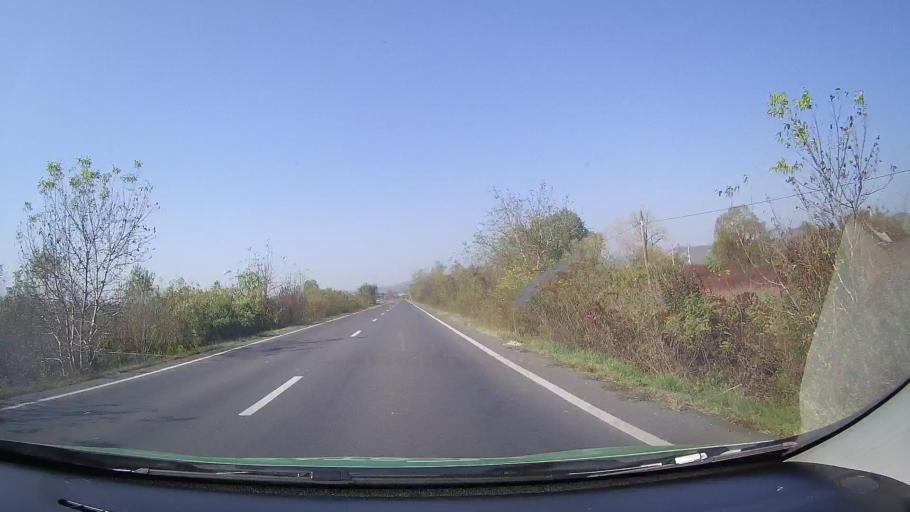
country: RO
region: Hunedoara
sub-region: Comuna Ilia
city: Ilia
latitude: 45.9415
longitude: 22.6388
